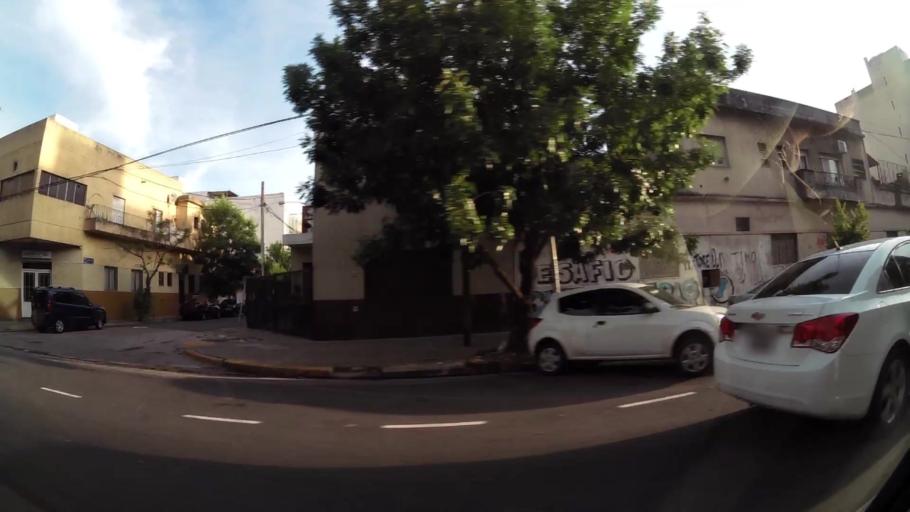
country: AR
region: Buenos Aires F.D.
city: Villa Santa Rita
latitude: -34.6337
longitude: -58.4308
